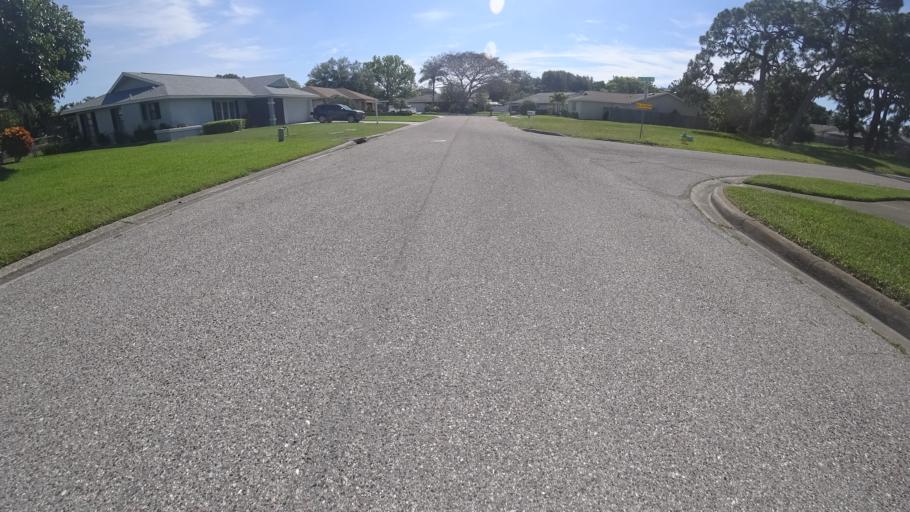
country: US
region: Florida
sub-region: Manatee County
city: West Bradenton
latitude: 27.5109
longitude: -82.6464
